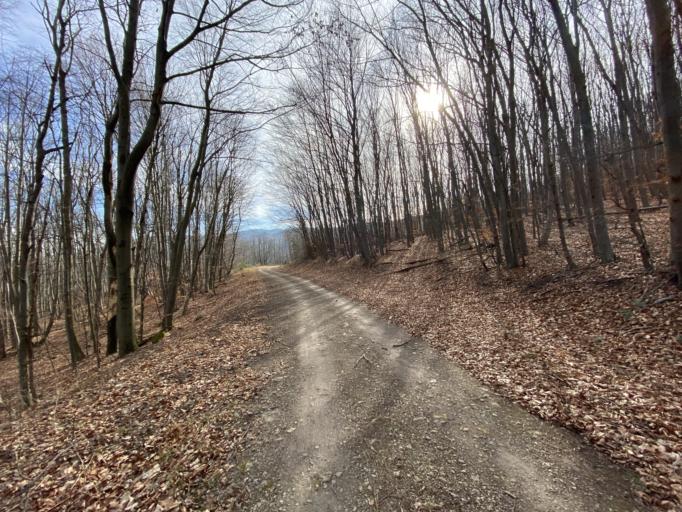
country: AT
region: Lower Austria
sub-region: Politischer Bezirk Baden
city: Heiligenkreuz
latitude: 48.0105
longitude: 16.1559
